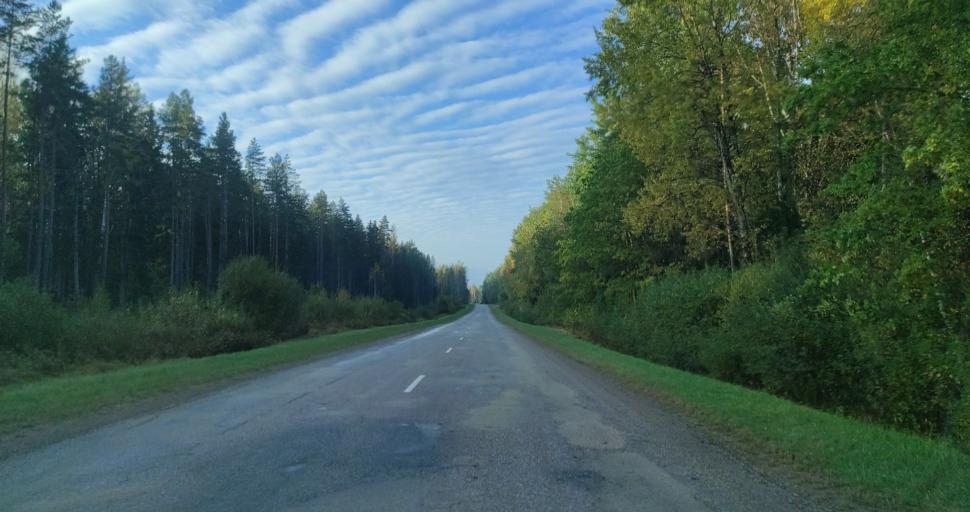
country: LV
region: Skrunda
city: Skrunda
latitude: 56.7995
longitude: 22.0051
